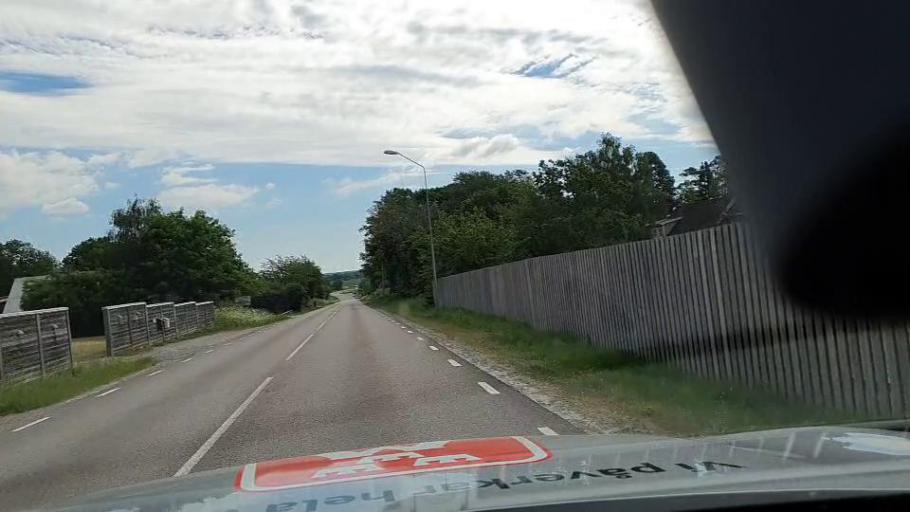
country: SE
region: Blekinge
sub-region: Karlskrona Kommun
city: Jaemjoe
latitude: 56.1672
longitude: 15.7517
